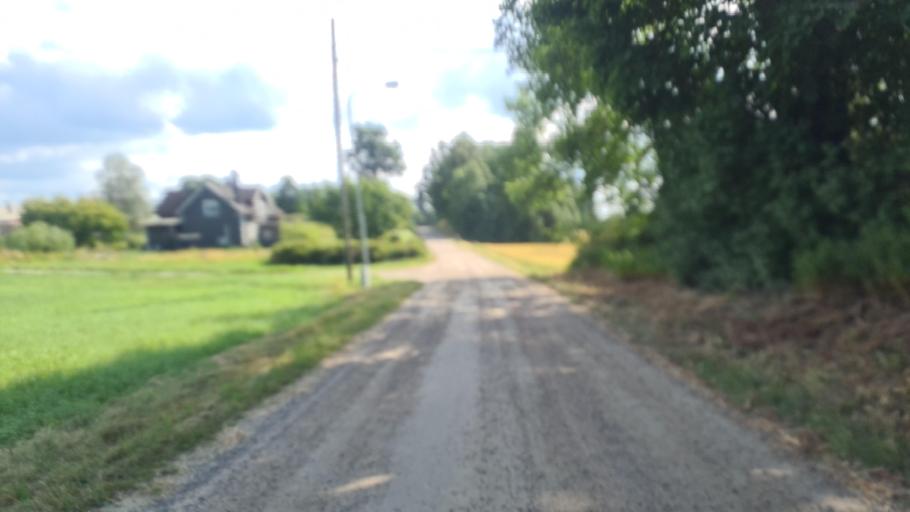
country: SE
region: Kronoberg
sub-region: Ljungby Kommun
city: Ljungby
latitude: 56.7345
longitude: 13.8718
